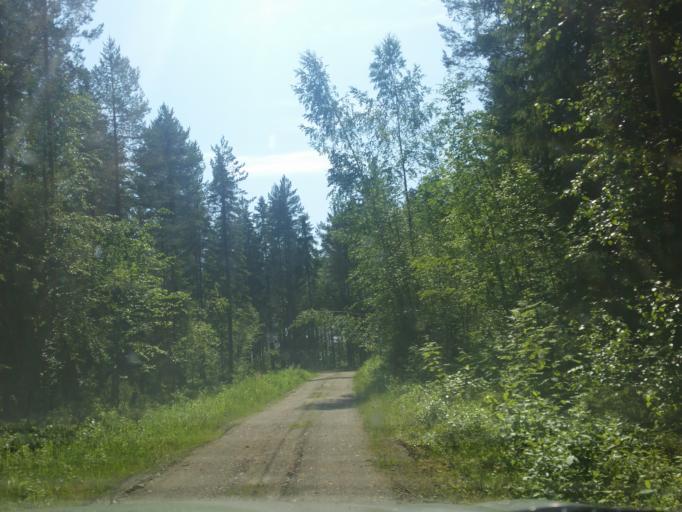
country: FI
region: Northern Savo
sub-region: Sisae-Savo
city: Tervo
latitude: 63.0710
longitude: 26.5970
